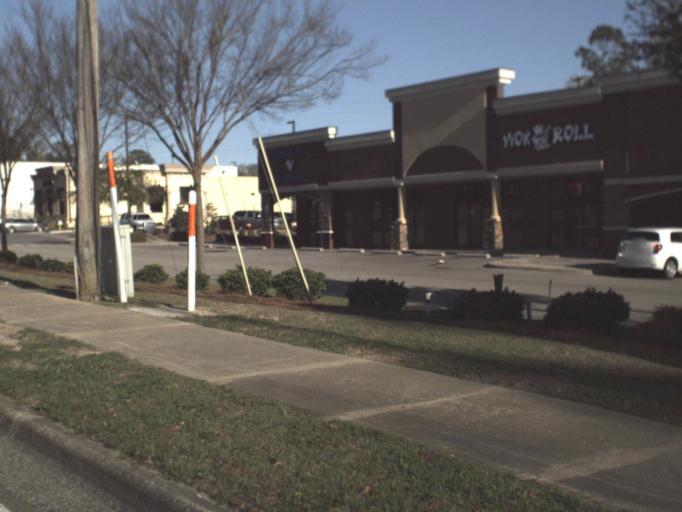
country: US
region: Florida
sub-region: Leon County
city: Tallahassee
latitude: 30.4591
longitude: -84.2304
